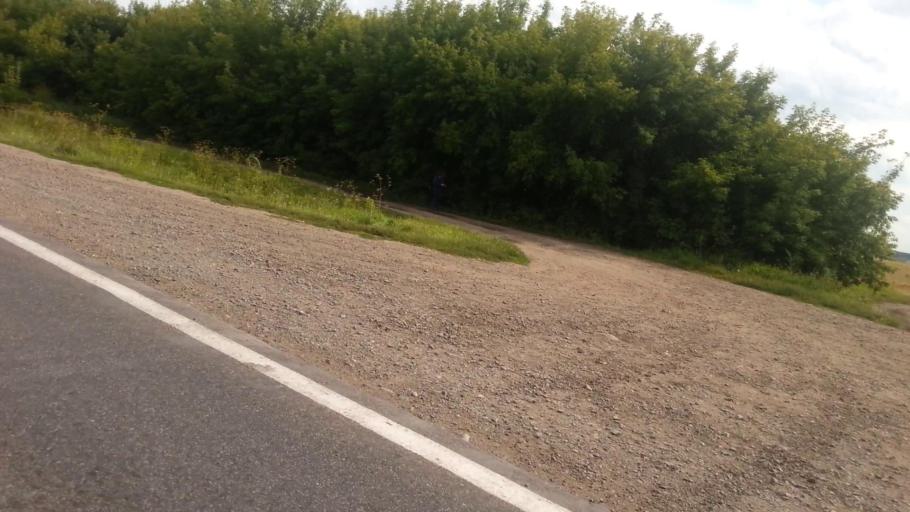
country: RU
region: Altai Krai
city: Nauchnyy Gorodok
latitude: 53.3566
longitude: 83.5079
